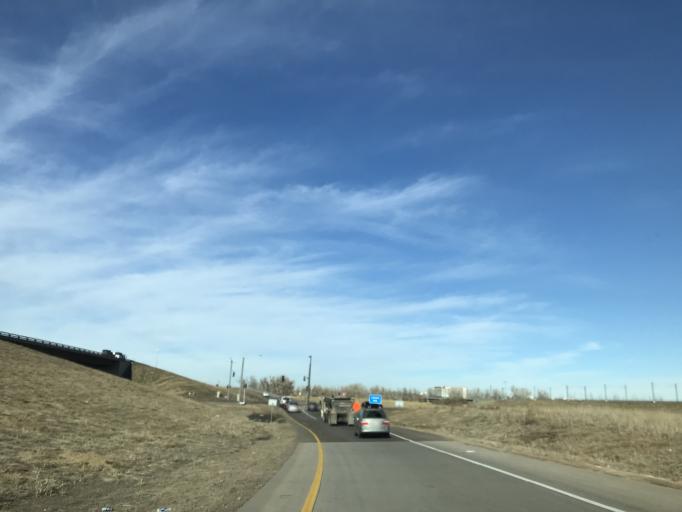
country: US
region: Colorado
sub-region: Adams County
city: Aurora
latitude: 39.7972
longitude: -104.7860
